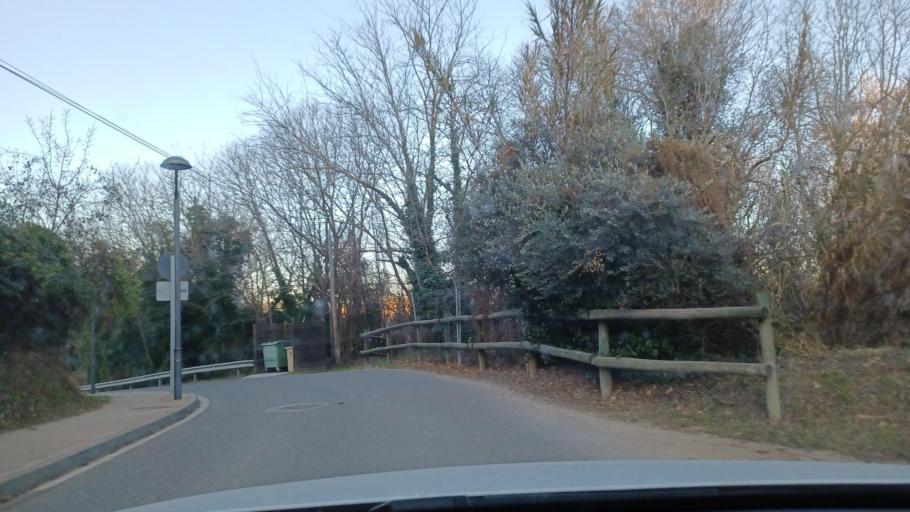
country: ES
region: Catalonia
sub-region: Provincia de Barcelona
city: Vilafranca del Penedes
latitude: 41.3612
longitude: 1.6723
